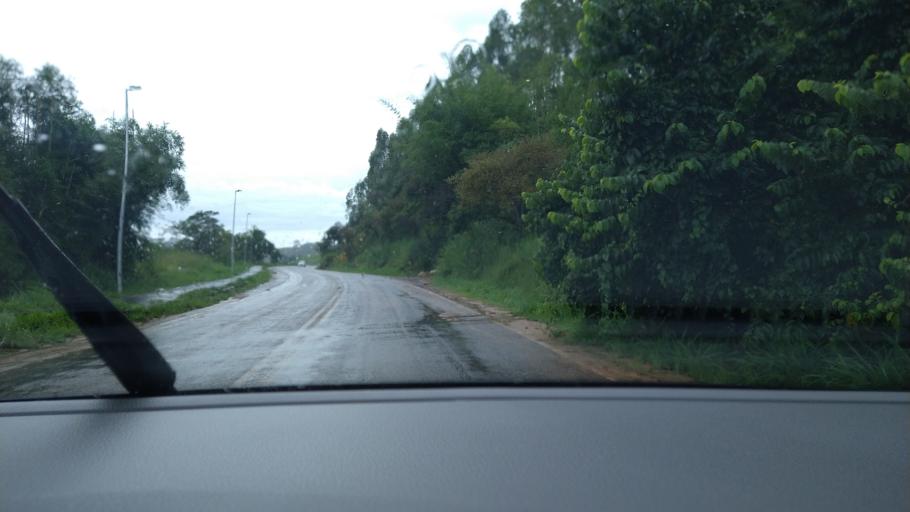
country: BR
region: Minas Gerais
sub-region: Ponte Nova
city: Ponte Nova
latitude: -20.3928
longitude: -42.9014
